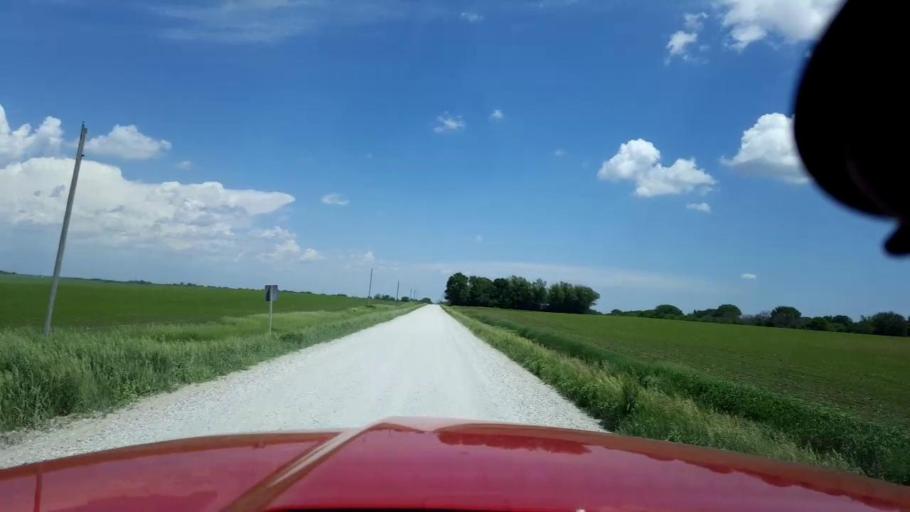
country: US
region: Iowa
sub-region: Boone County
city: Boone
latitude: 42.0493
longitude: -93.7743
